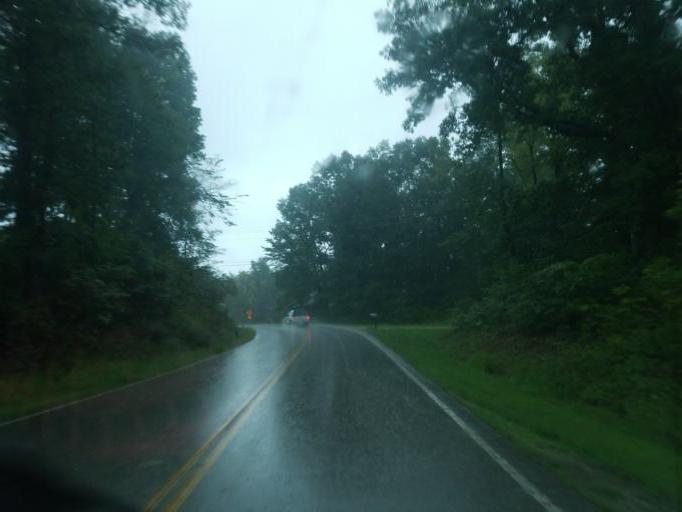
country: US
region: Kentucky
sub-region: Carter County
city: Olive Hill
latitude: 38.3429
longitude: -83.2015
